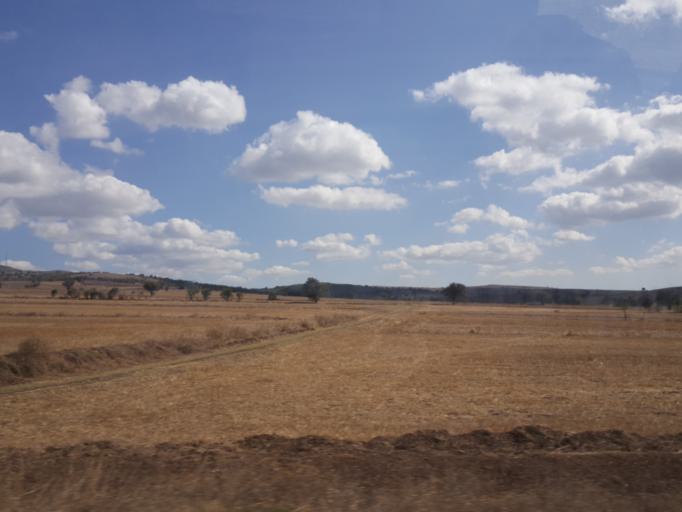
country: TR
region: Tokat
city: Camlibel
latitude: 40.2024
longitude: 36.4737
